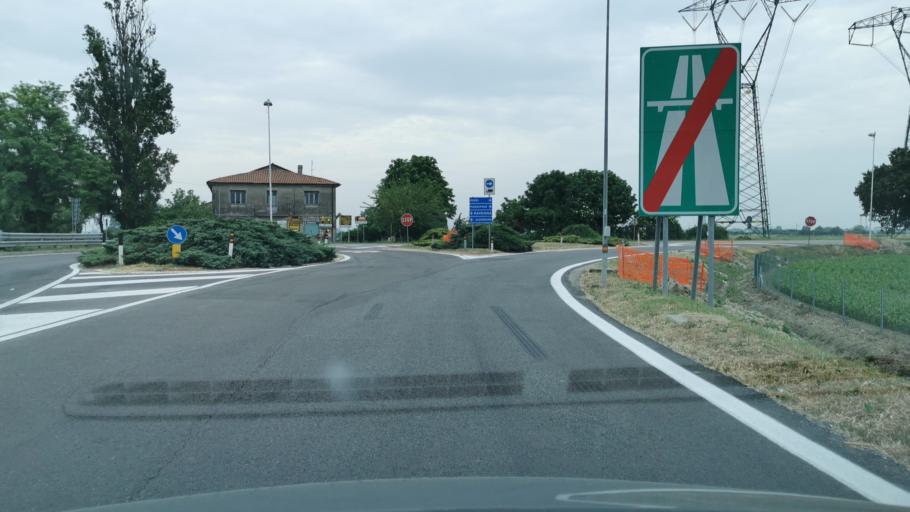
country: IT
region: Emilia-Romagna
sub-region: Provincia di Ravenna
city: Fornace Zarattini
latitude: 44.4136
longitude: 12.1268
